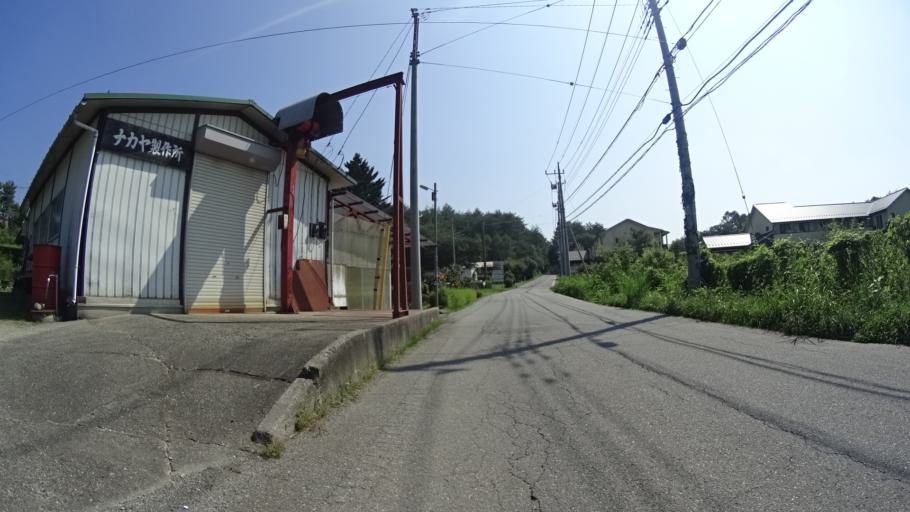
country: JP
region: Yamanashi
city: Nirasaki
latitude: 35.8710
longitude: 138.3371
